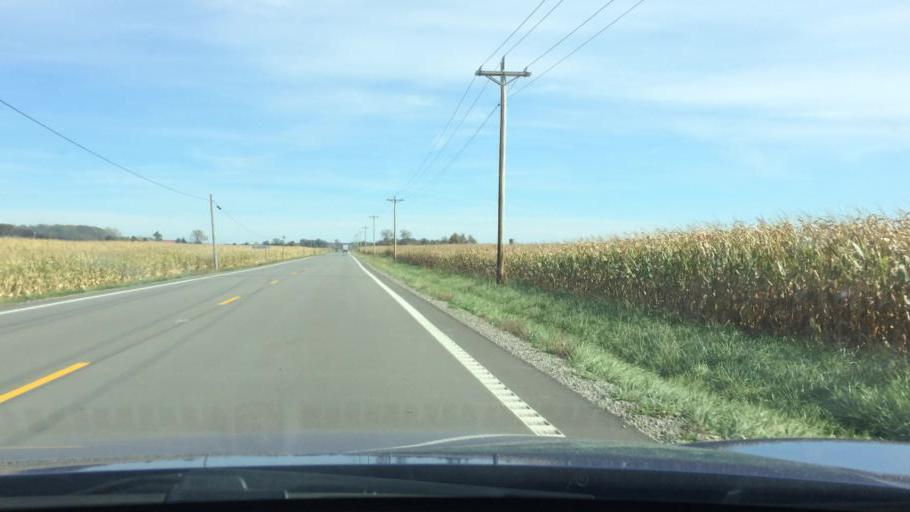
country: US
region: Ohio
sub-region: Logan County
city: Russells Point
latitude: 40.4425
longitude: -83.8533
